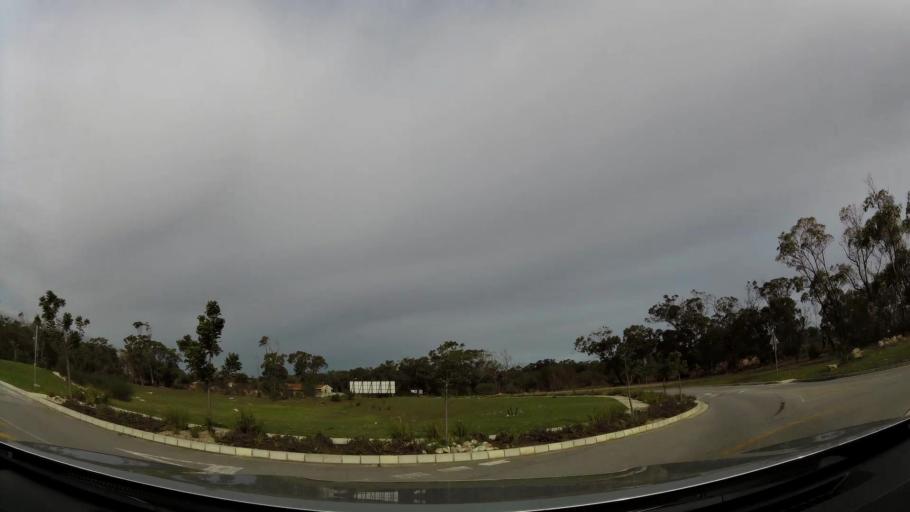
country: ZA
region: Eastern Cape
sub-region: Nelson Mandela Bay Metropolitan Municipality
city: Port Elizabeth
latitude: -33.9335
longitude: 25.4902
